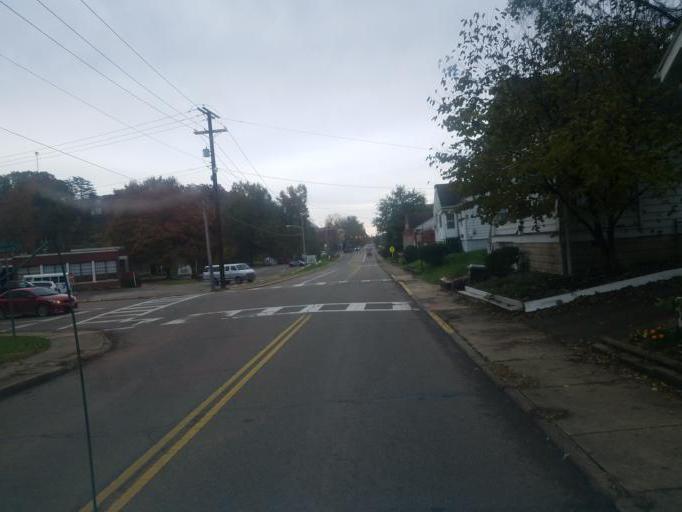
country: US
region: Ohio
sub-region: Washington County
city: Marietta
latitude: 39.4209
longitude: -81.4498
